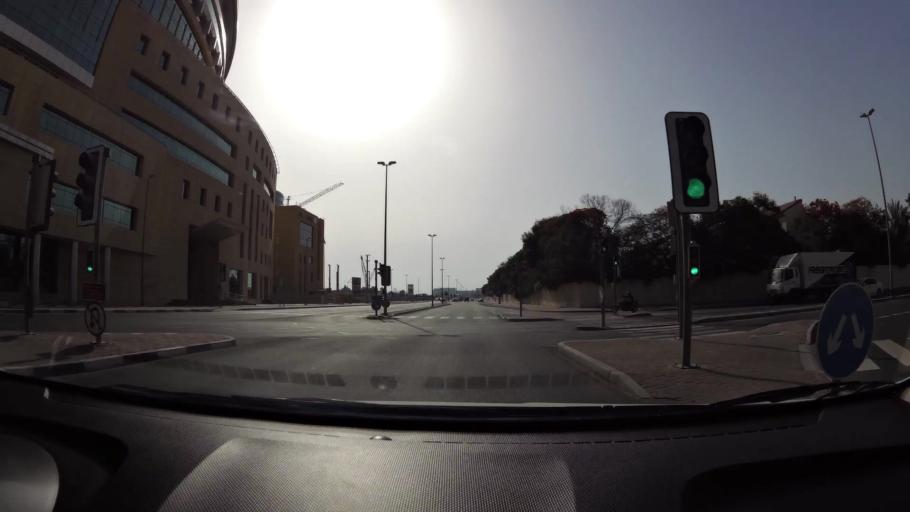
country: AE
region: Ash Shariqah
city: Sharjah
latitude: 25.2348
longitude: 55.3562
